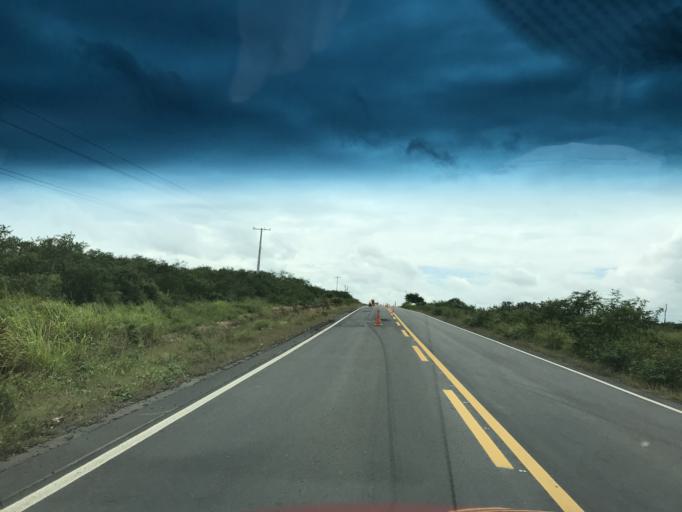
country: BR
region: Bahia
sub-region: Castro Alves
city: Castro Alves
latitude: -12.6856
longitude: -39.3101
